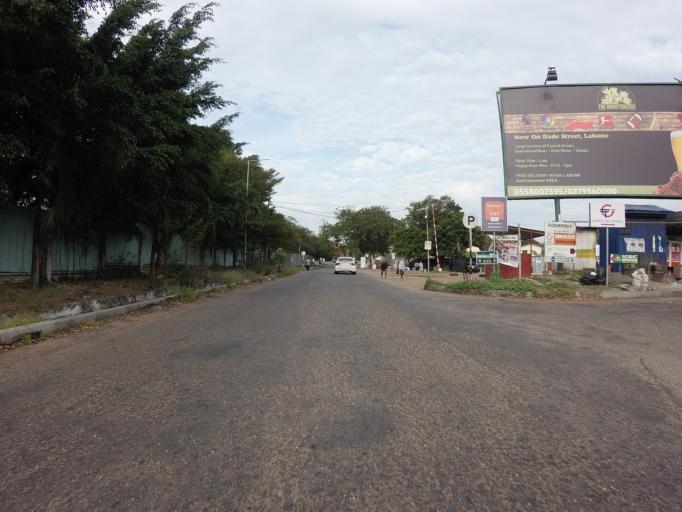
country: GH
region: Greater Accra
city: Accra
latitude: 5.5776
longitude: -0.1710
